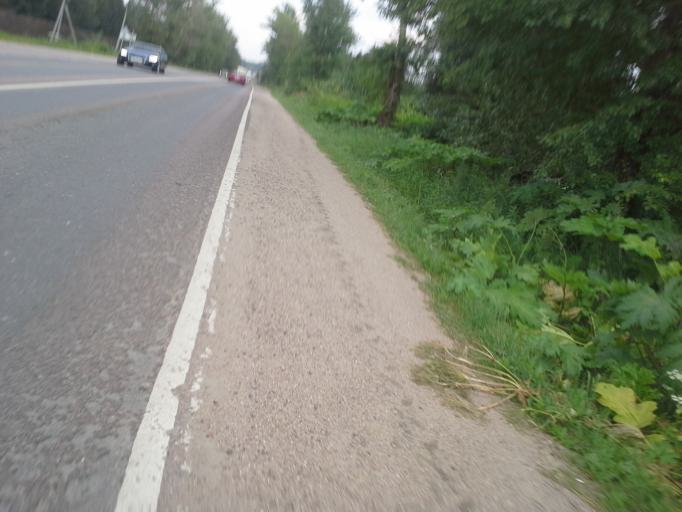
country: RU
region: Moskovskaya
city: Istra
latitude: 55.9302
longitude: 36.9397
